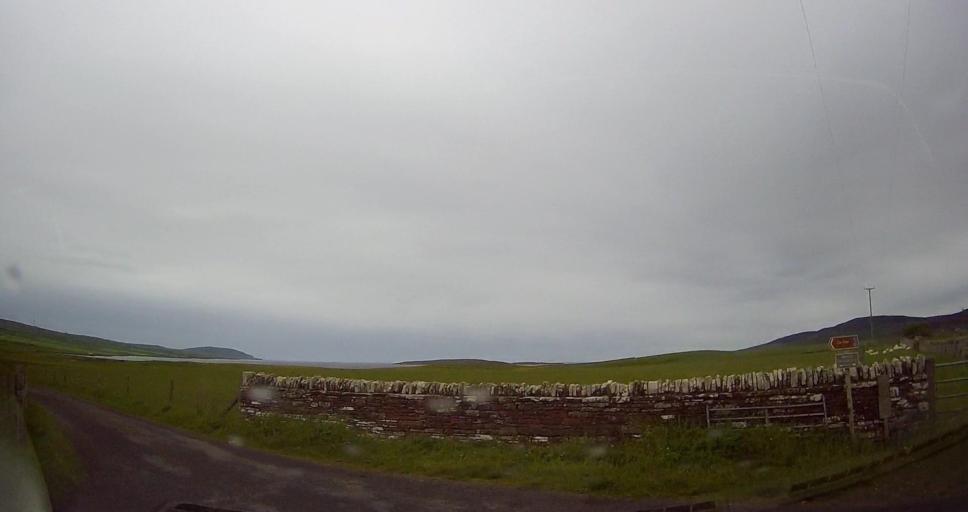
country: GB
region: Scotland
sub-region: Orkney Islands
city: Orkney
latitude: 59.1168
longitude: -3.0755
